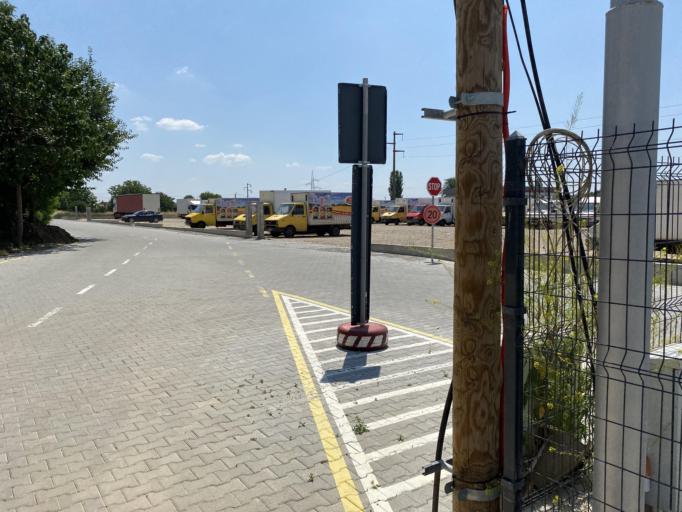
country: MK
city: Radishani
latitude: 42.0466
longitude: 21.4471
